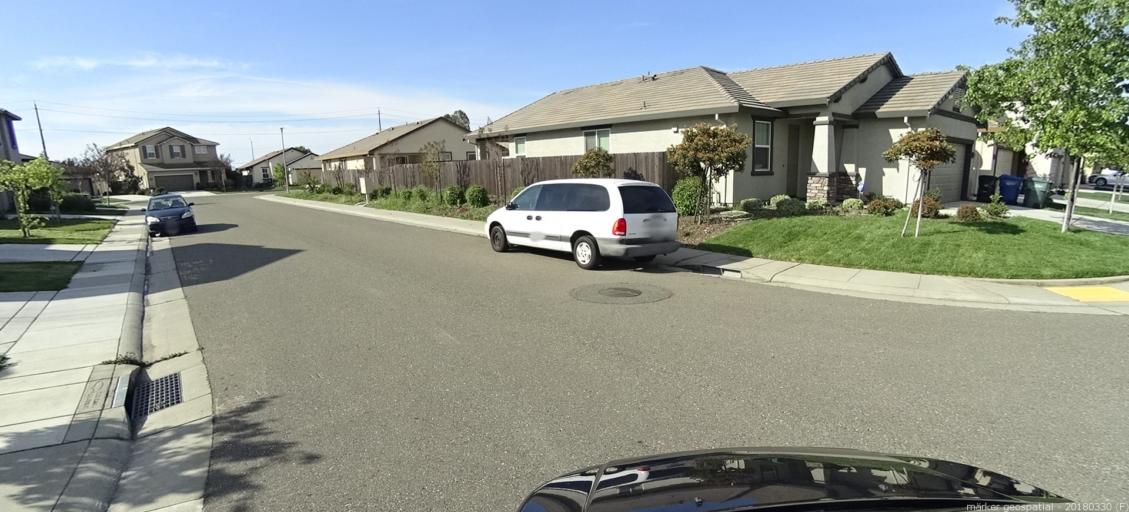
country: US
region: California
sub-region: Sacramento County
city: Vineyard
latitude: 38.4828
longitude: -121.3424
